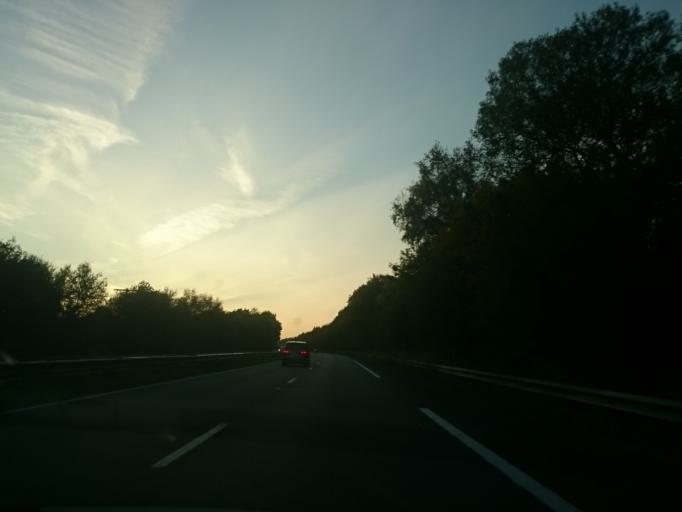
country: FR
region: Brittany
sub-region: Departement du Finistere
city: Melgven
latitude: 47.9158
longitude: -3.8738
